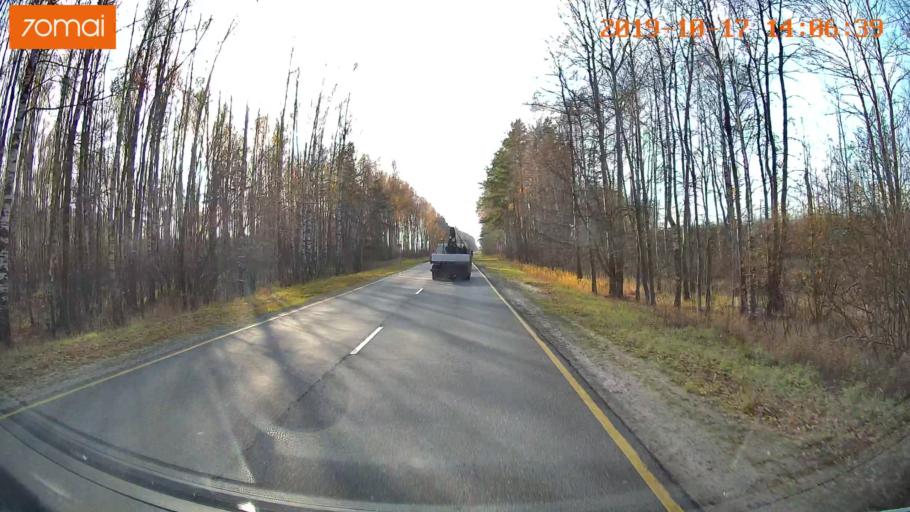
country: RU
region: Rjazan
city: Spas-Klepiki
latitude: 55.1117
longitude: 40.1022
